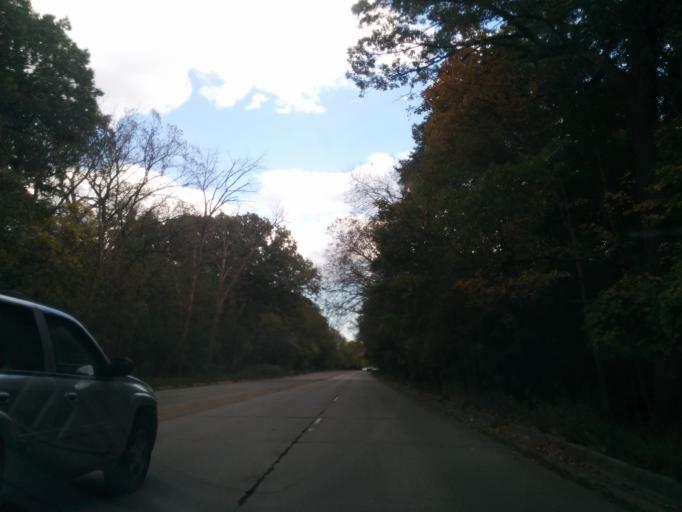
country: US
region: Illinois
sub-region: Cook County
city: Park Ridge
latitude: 41.9909
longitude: -87.8494
